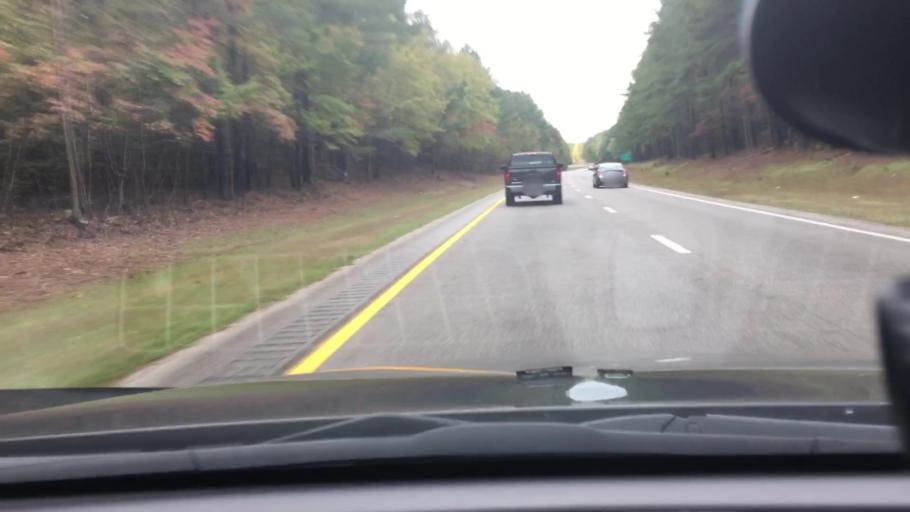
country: US
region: North Carolina
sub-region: Wake County
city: Zebulon
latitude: 35.7955
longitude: -78.1642
